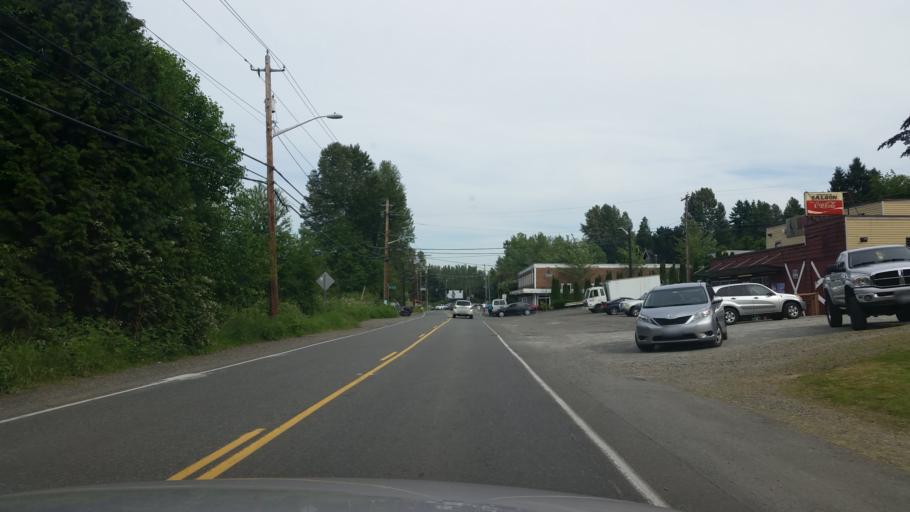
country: US
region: Washington
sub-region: King County
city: Woodinville
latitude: 47.7542
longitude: -122.1726
